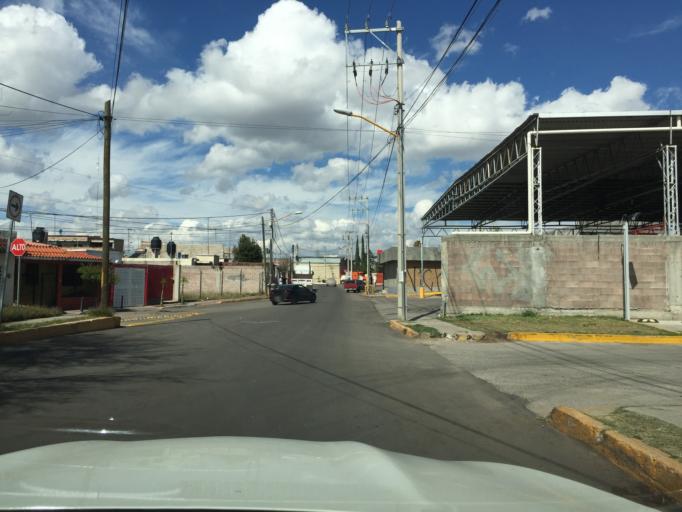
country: MX
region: Aguascalientes
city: Jesus Gomez Portugal
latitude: 21.9913
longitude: -102.2894
